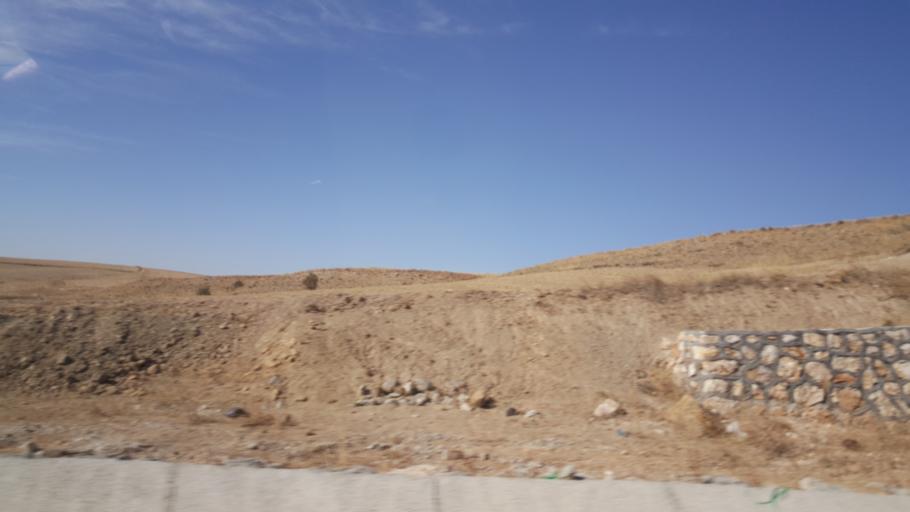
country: TR
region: Ankara
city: Haymana
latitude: 39.4915
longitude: 32.5567
